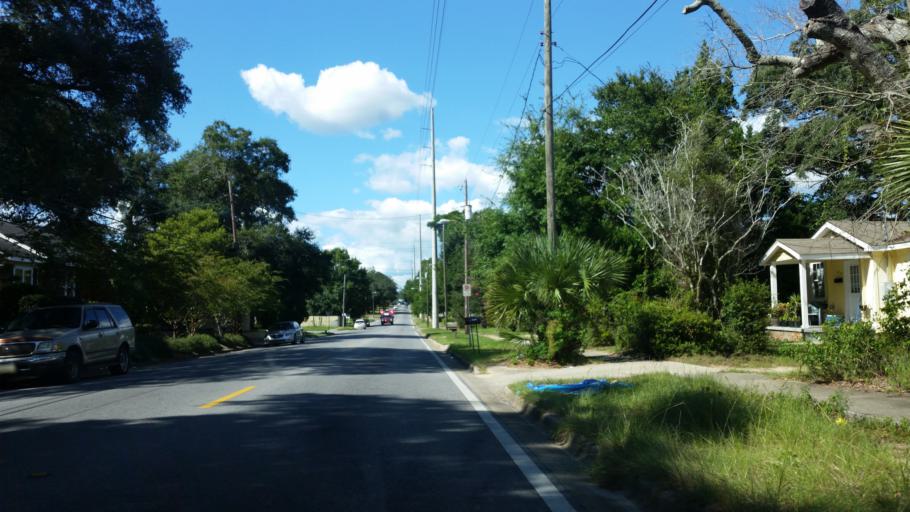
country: US
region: Florida
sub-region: Escambia County
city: Pensacola
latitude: 30.4245
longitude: -87.2298
